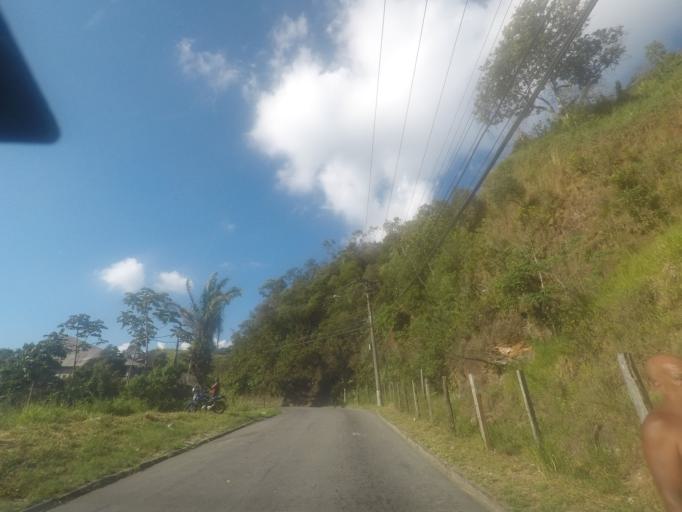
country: BR
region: Rio de Janeiro
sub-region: Petropolis
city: Petropolis
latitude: -22.5057
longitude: -43.1555
